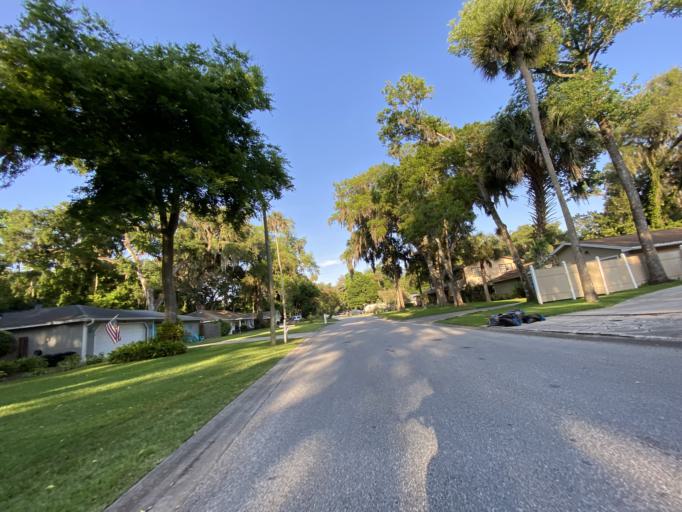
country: US
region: Florida
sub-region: Volusia County
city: Port Orange
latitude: 29.1452
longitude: -81.0111
